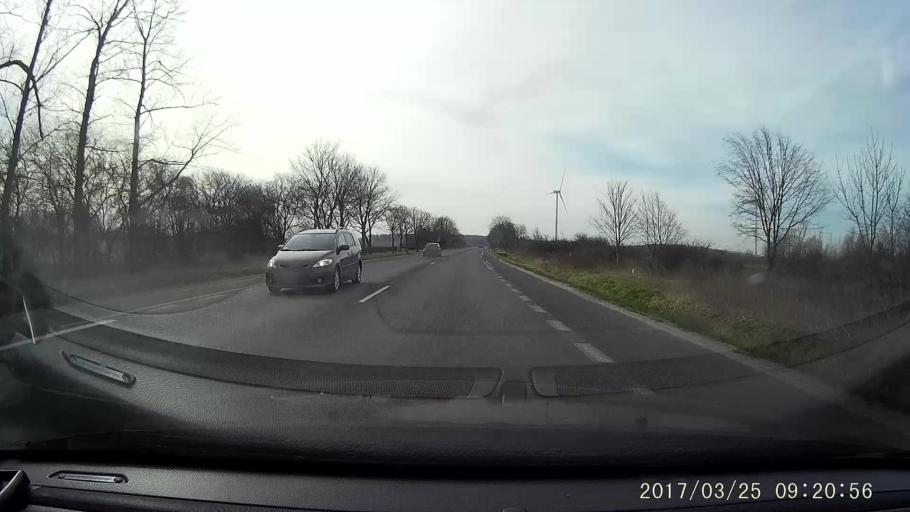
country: PL
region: Lower Silesian Voivodeship
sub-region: Powiat zgorzelecki
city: Sulikow
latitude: 51.0910
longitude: 15.0228
